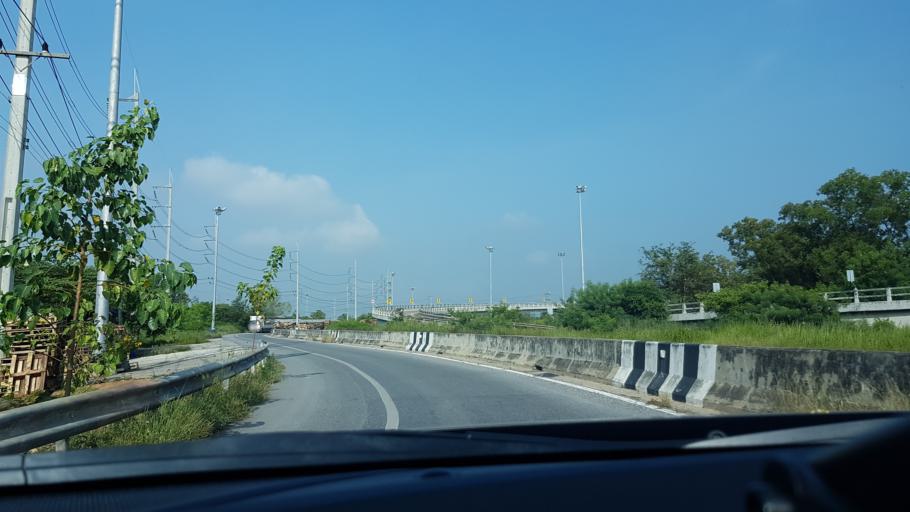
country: TH
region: Phra Nakhon Si Ayutthaya
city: Bang Pa-in
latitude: 14.1544
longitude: 100.5679
